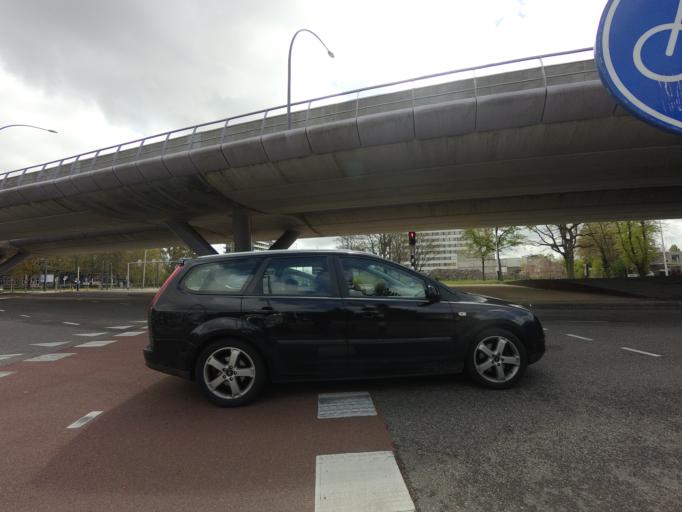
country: NL
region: Utrecht
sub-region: Gemeente Utrecht
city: Utrecht
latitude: 52.0810
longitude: 5.0900
